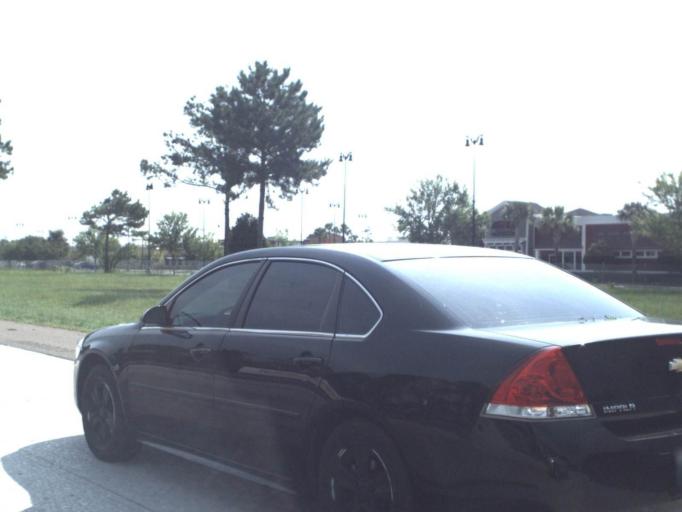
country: US
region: Florida
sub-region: Duval County
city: Jacksonville
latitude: 30.4749
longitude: -81.6449
